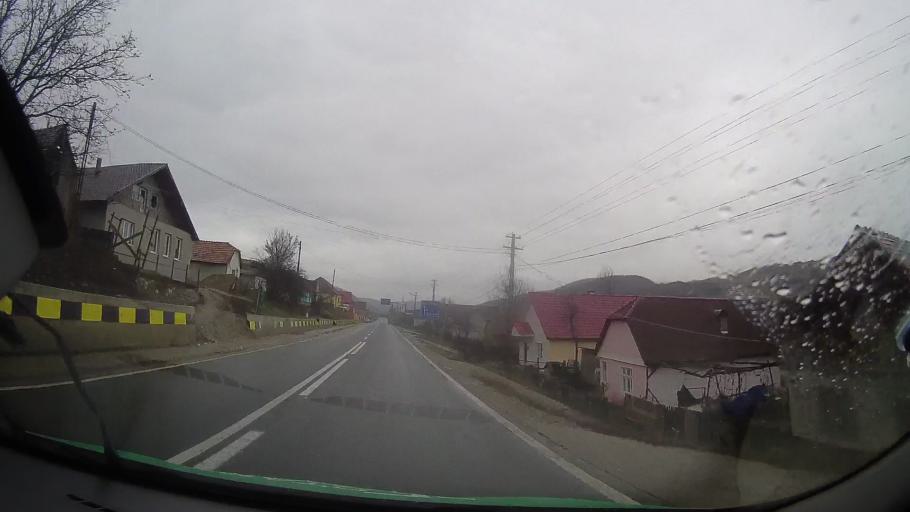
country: RO
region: Bistrita-Nasaud
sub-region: Comuna Galatii Bistritei
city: Galatii Bistritei
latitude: 46.9497
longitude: 24.4515
